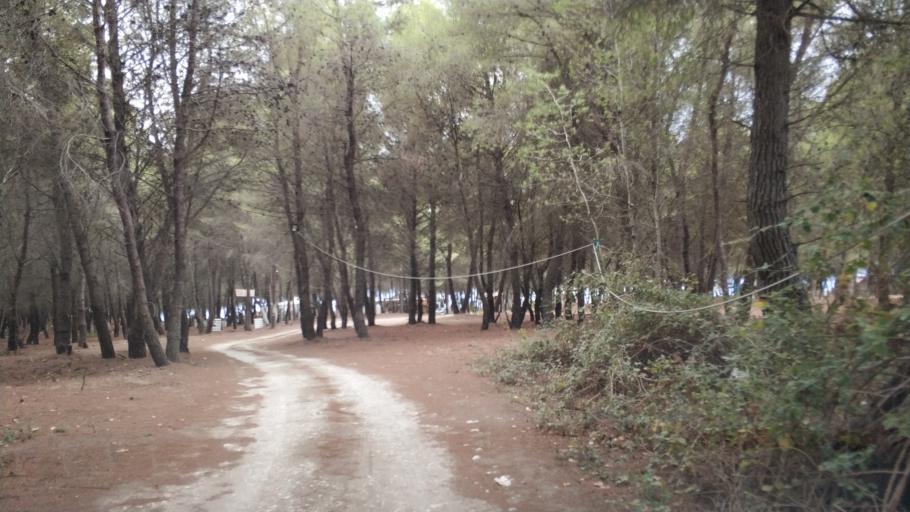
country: AL
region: Vlore
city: Vlore
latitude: 40.5025
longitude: 19.4197
